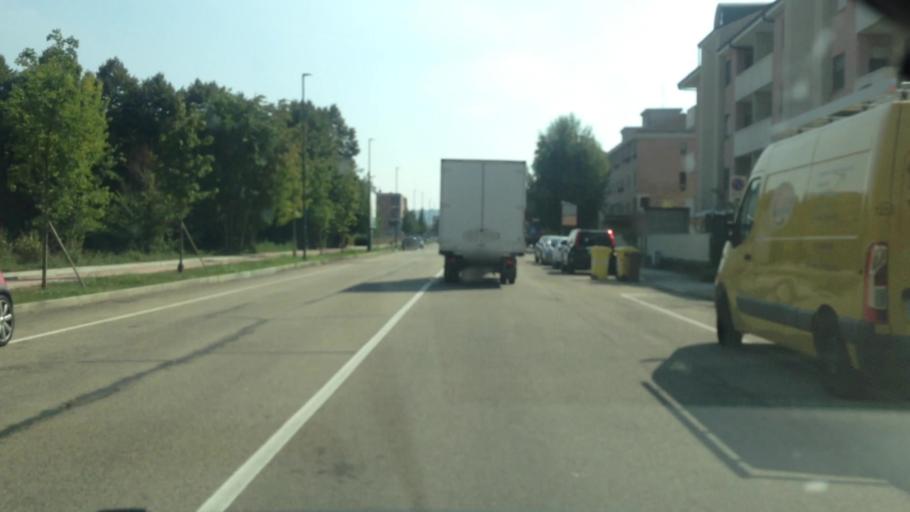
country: IT
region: Piedmont
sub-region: Provincia di Asti
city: Asti
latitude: 44.9032
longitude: 8.2215
